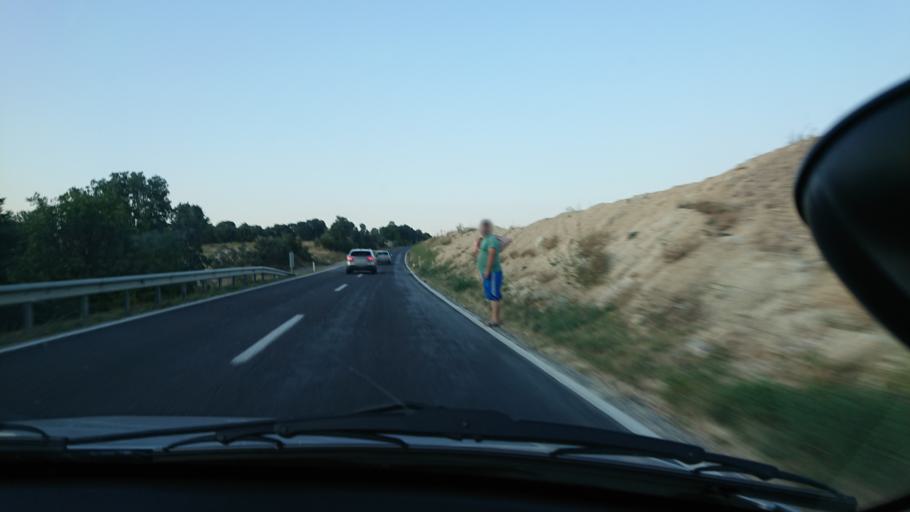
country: TR
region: Usak
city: Gure
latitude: 38.7590
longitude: 29.1985
